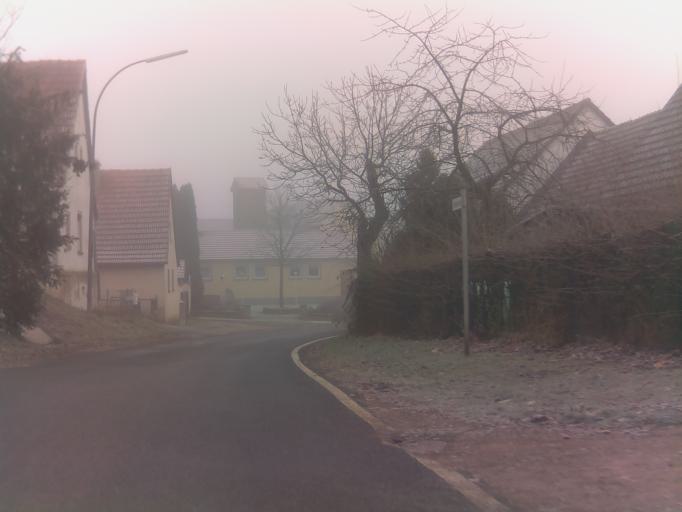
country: DE
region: Bavaria
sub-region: Regierungsbezirk Unterfranken
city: Michelau
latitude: 49.9372
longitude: 10.4354
